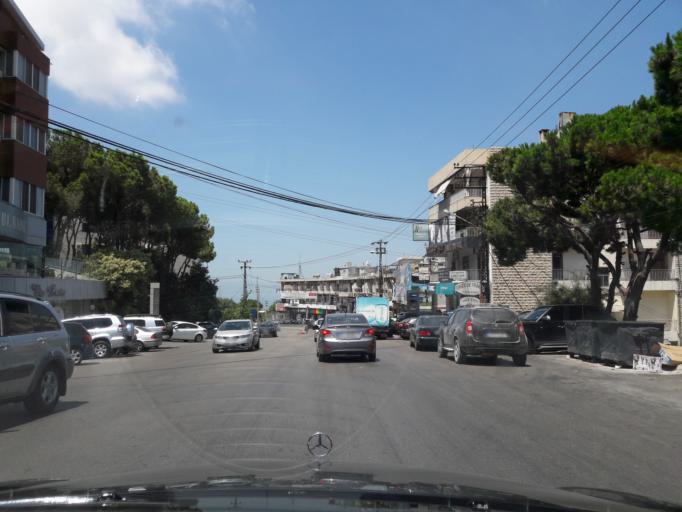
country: LB
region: Mont-Liban
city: Djounie
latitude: 33.9271
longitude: 35.6277
